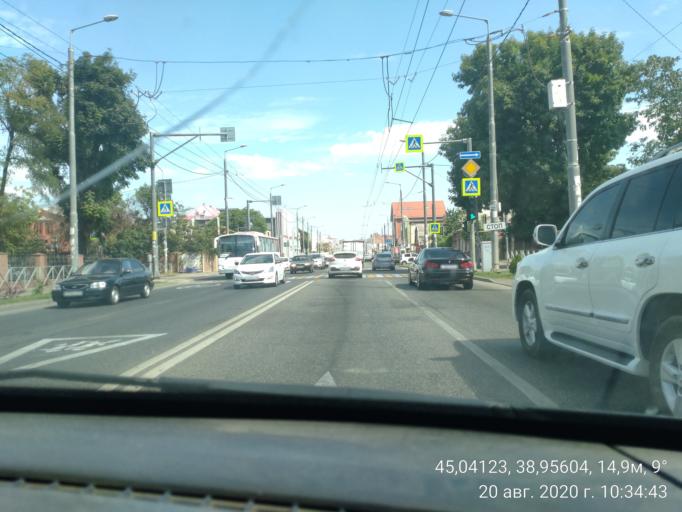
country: RU
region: Krasnodarskiy
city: Krasnodar
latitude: 45.0414
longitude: 38.9569
